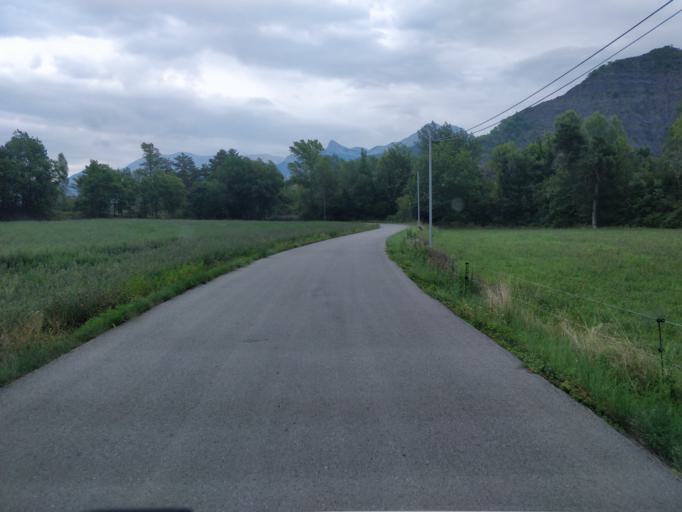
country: FR
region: Provence-Alpes-Cote d'Azur
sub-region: Departement des Alpes-de-Haute-Provence
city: Digne-les-Bains
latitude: 44.1329
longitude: 6.2665
